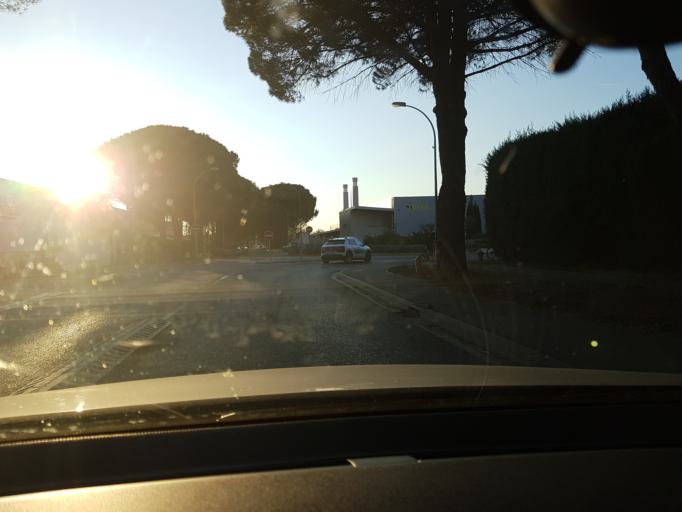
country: FR
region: Provence-Alpes-Cote d'Azur
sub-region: Departement des Bouches-du-Rhone
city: Rousset
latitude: 43.4693
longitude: 5.6070
